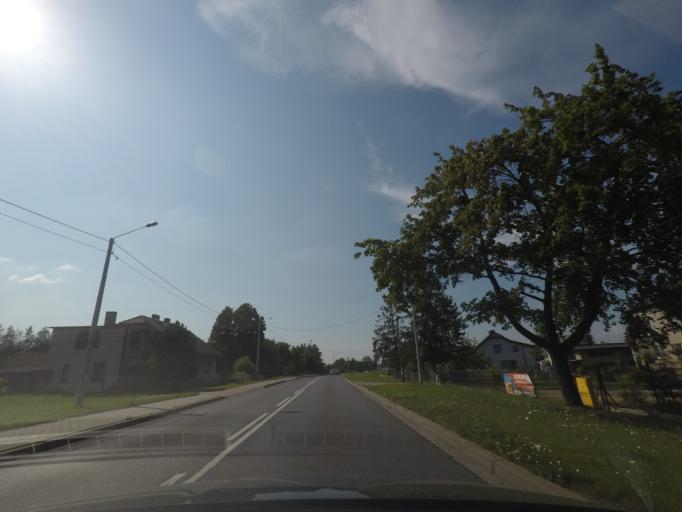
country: PL
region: Silesian Voivodeship
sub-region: Powiat pszczynski
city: Radostowice
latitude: 50.0047
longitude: 18.8737
